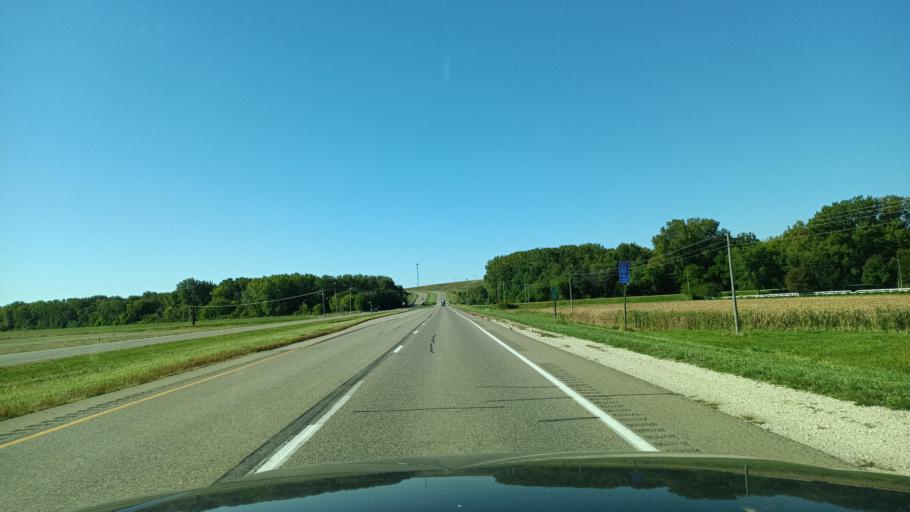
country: US
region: Iowa
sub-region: Lee County
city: Fort Madison
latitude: 40.6989
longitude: -91.2431
